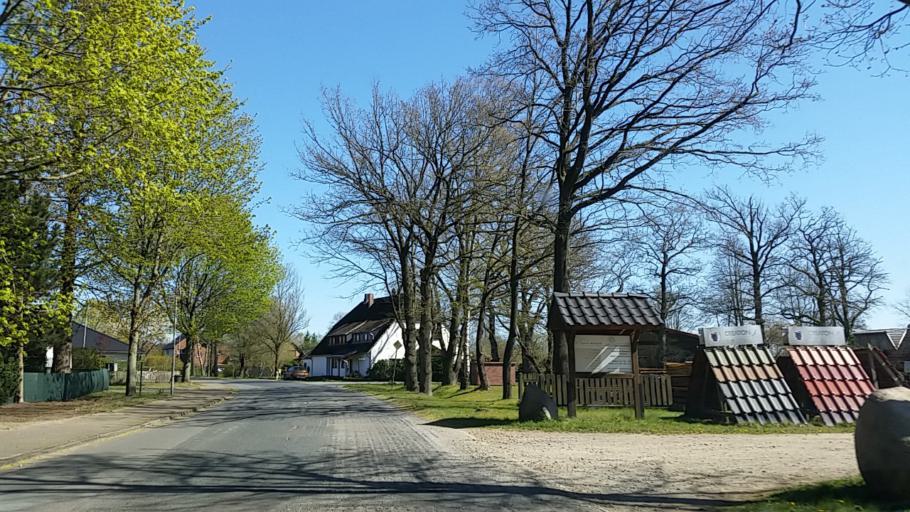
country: DE
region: Lower Saxony
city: Handeloh
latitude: 53.1851
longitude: 9.8318
